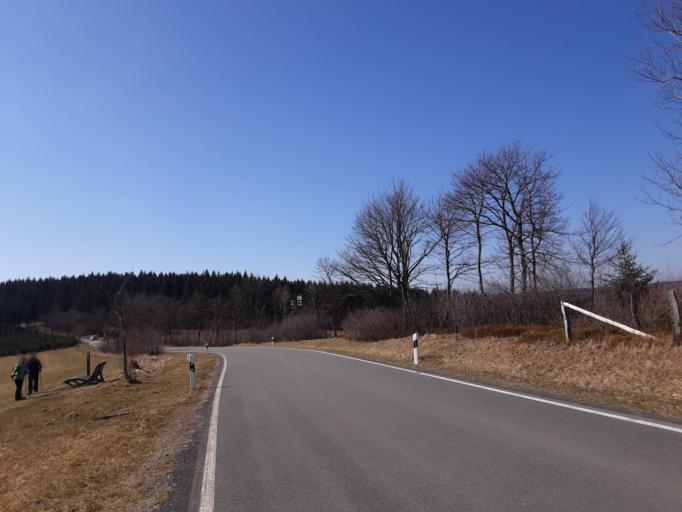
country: DE
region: North Rhine-Westphalia
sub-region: Regierungsbezirk Arnsberg
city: Winterberg
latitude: 51.1980
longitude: 8.4641
